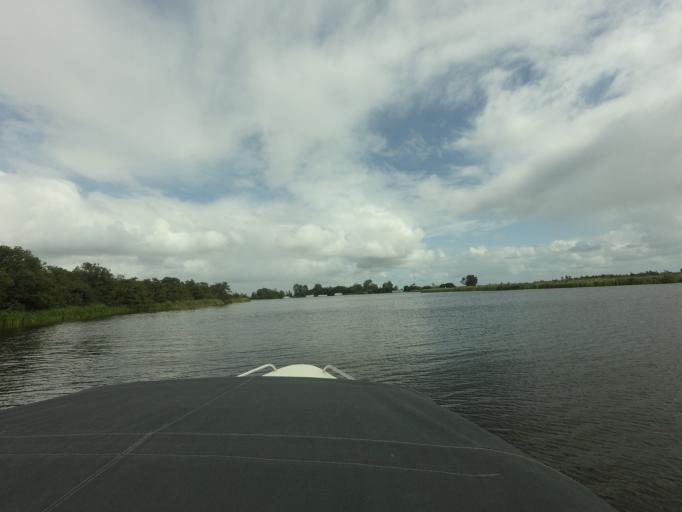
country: NL
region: Friesland
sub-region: Gemeente Boarnsterhim
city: Warten
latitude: 53.1174
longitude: 5.9419
